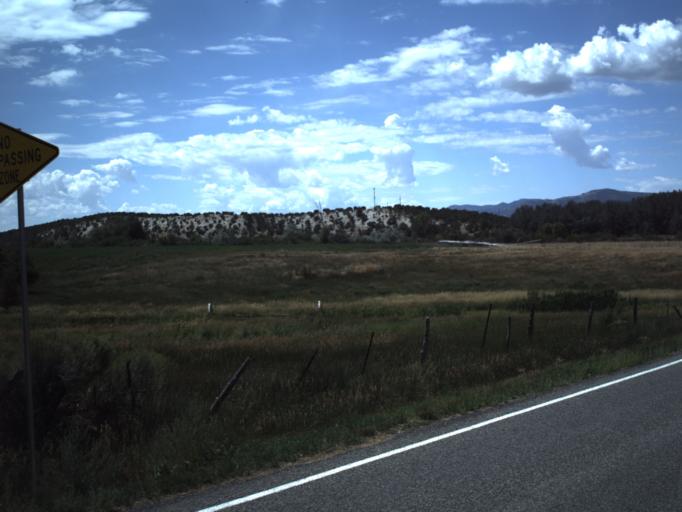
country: US
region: Utah
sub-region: Sanpete County
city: Mount Pleasant
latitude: 39.4818
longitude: -111.5070
